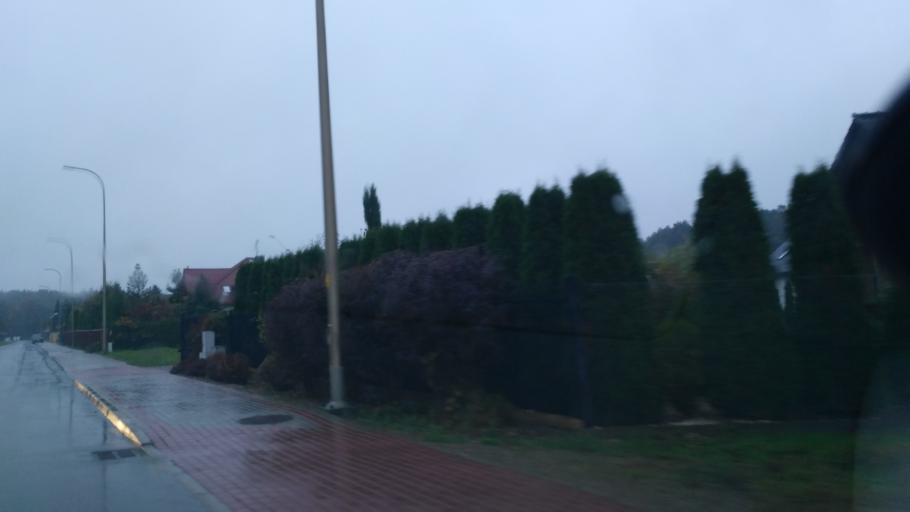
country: PL
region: Subcarpathian Voivodeship
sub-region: Powiat krosnienski
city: Kroscienko Wyzne
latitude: 49.6693
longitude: 21.8038
